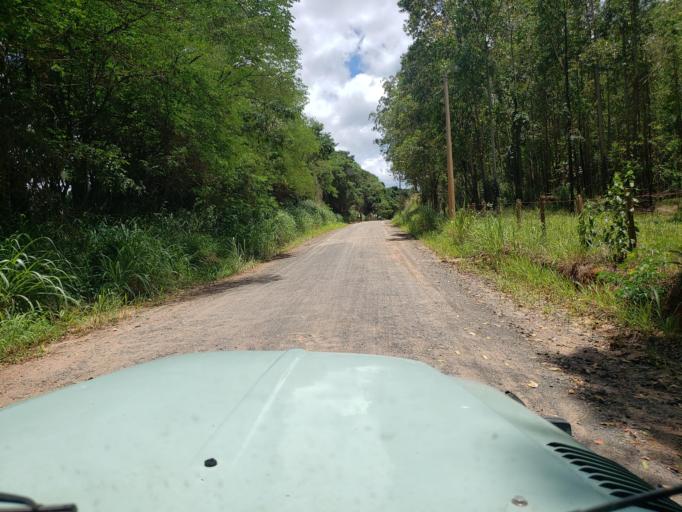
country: BR
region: Sao Paulo
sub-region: Moji-Guacu
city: Mogi-Gaucu
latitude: -22.2545
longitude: -46.8490
